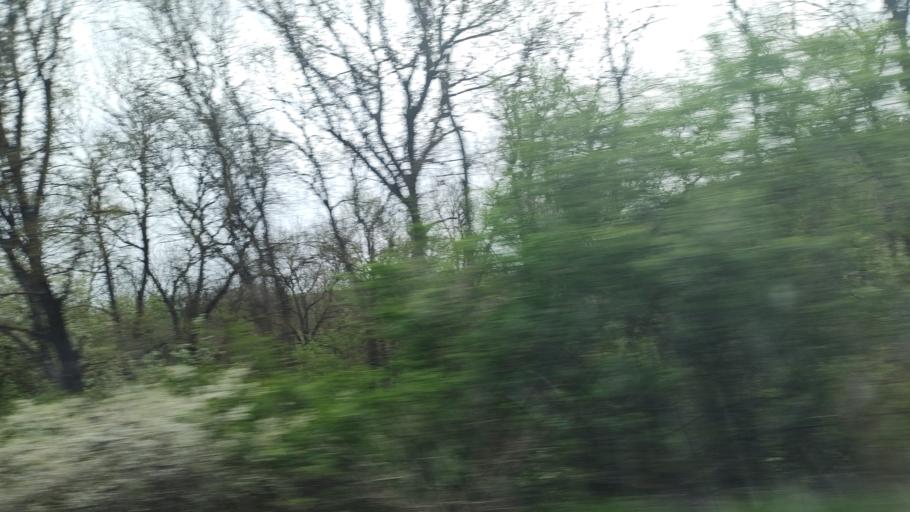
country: RO
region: Constanta
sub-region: Oras Murfatlar
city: Siminoc
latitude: 44.1565
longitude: 28.3799
